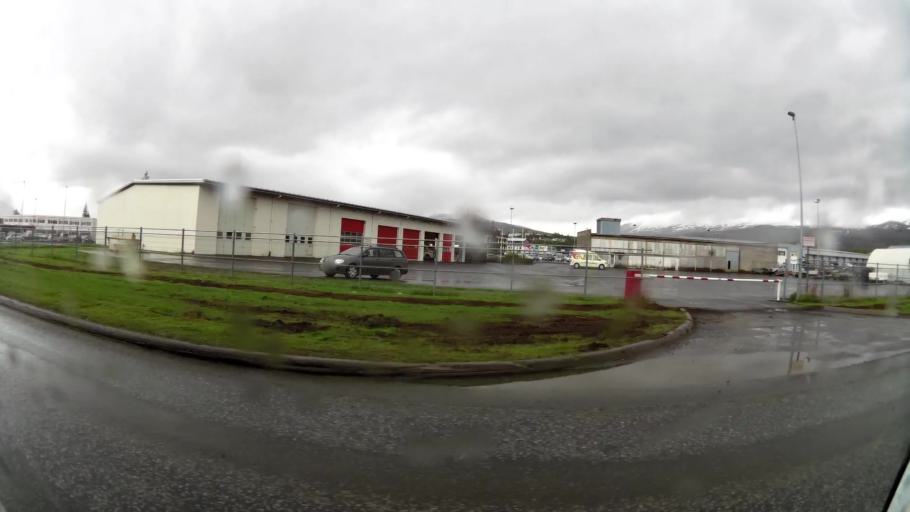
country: IS
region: Northeast
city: Akureyri
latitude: 65.6919
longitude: -18.0937
